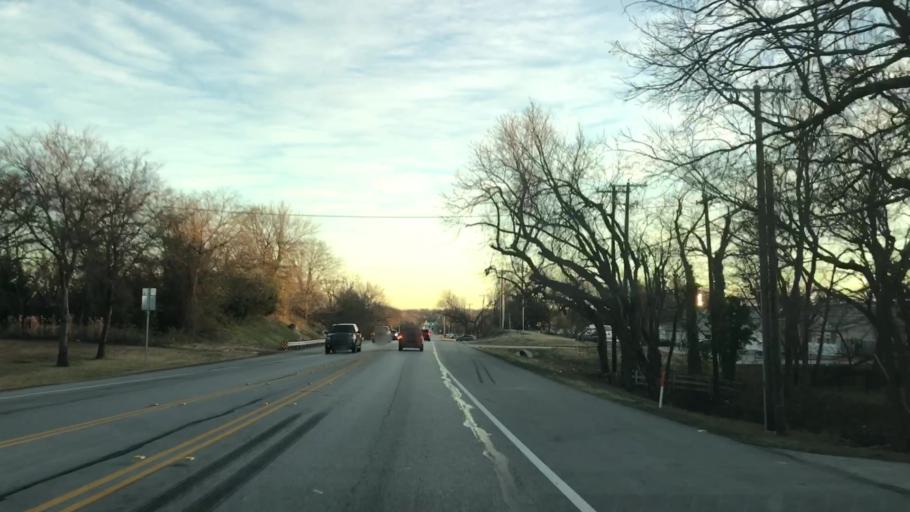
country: US
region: Texas
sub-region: Rockwall County
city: Rockwall
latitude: 32.9538
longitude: -96.4635
